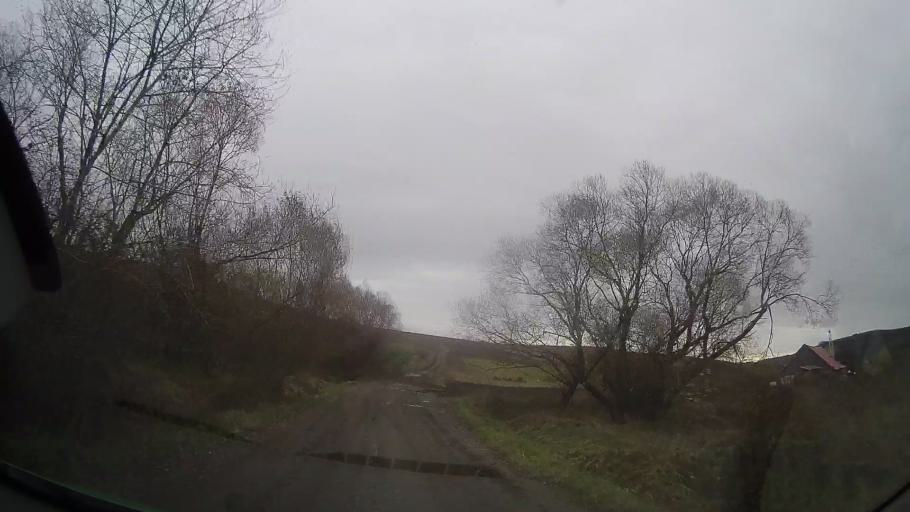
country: RO
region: Mures
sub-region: Comuna Bala
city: Bala
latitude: 46.6947
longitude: 24.4893
